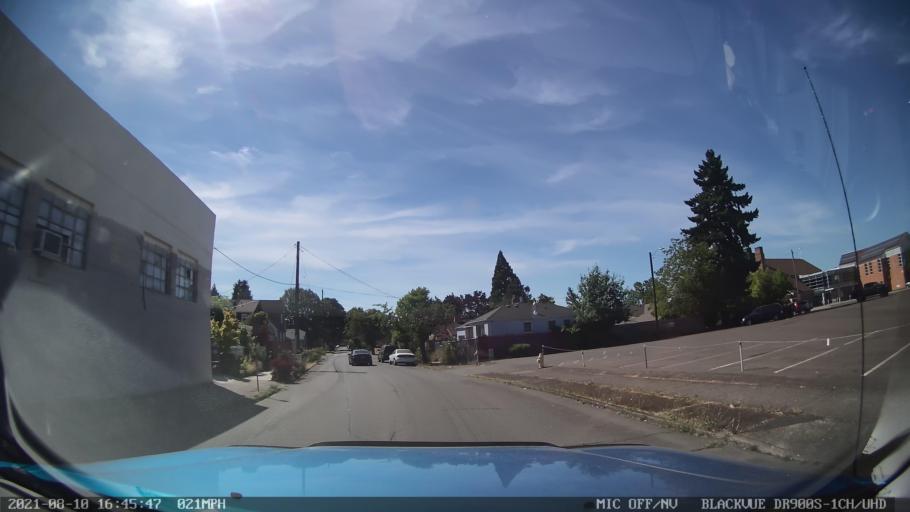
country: US
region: Oregon
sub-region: Marion County
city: Salem
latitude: 44.9577
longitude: -123.0199
